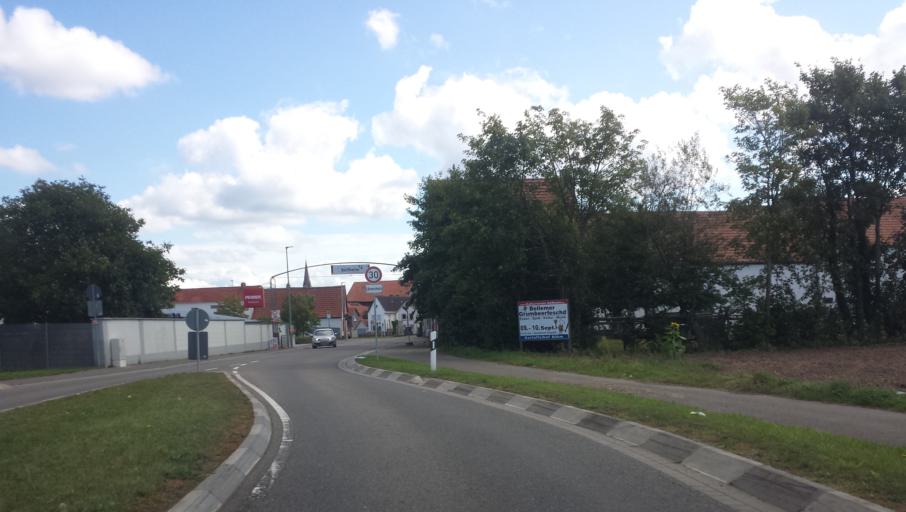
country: DE
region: Rheinland-Pfalz
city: Bellheim
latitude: 49.1915
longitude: 8.2695
